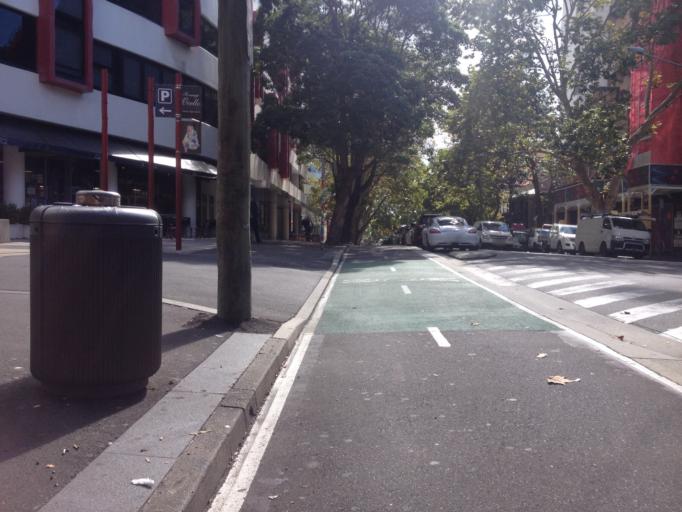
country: AU
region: New South Wales
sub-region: City of Sydney
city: Darlinghurst
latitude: -33.8834
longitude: 151.2161
